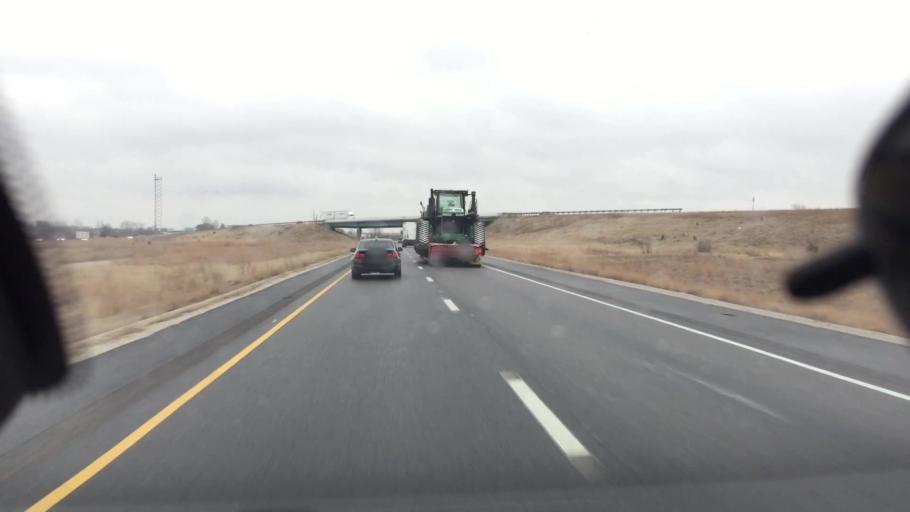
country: US
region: Illinois
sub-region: Tazewell County
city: East Peoria
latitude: 40.6347
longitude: -89.5223
